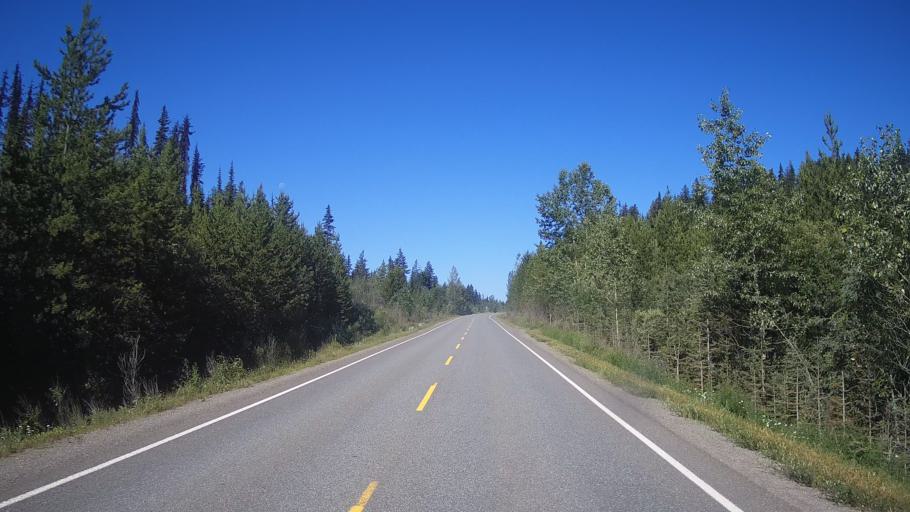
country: CA
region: British Columbia
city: Kamloops
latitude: 51.4966
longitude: -120.3871
